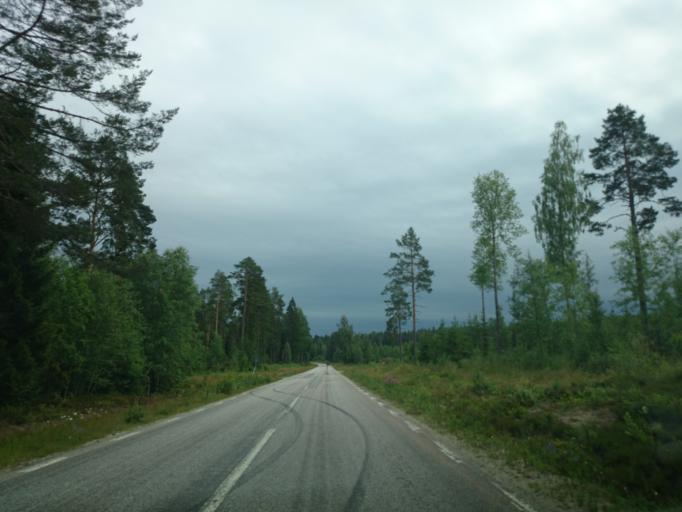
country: SE
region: Vaesternorrland
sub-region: Sundsvalls Kommun
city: Njurundabommen
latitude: 62.2305
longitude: 17.4062
